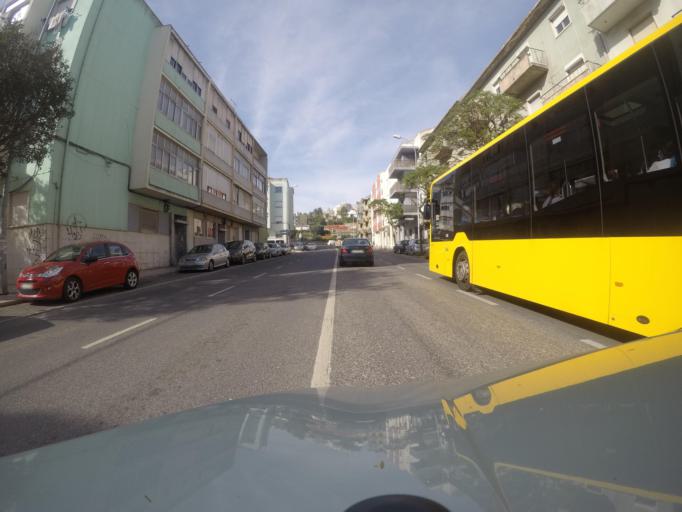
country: PT
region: Lisbon
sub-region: Amadora
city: Amadora
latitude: 38.7618
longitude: -9.2286
